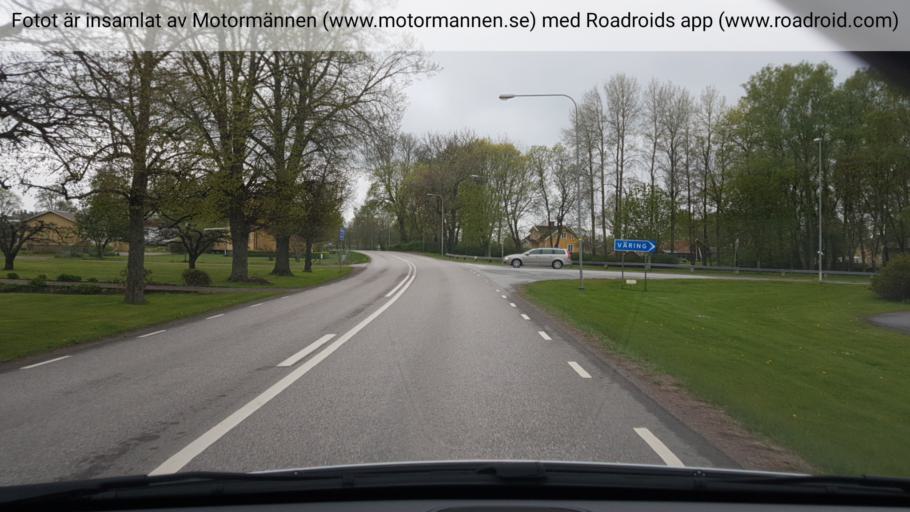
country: SE
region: Vaestra Goetaland
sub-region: Skovde Kommun
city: Stopen
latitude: 58.5109
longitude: 13.9713
